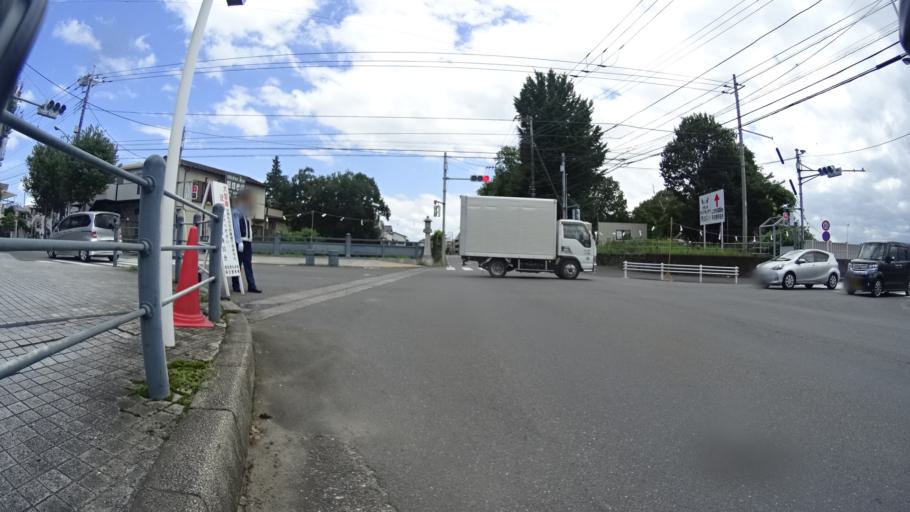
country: JP
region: Tokyo
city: Fussa
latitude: 35.7358
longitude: 139.3263
